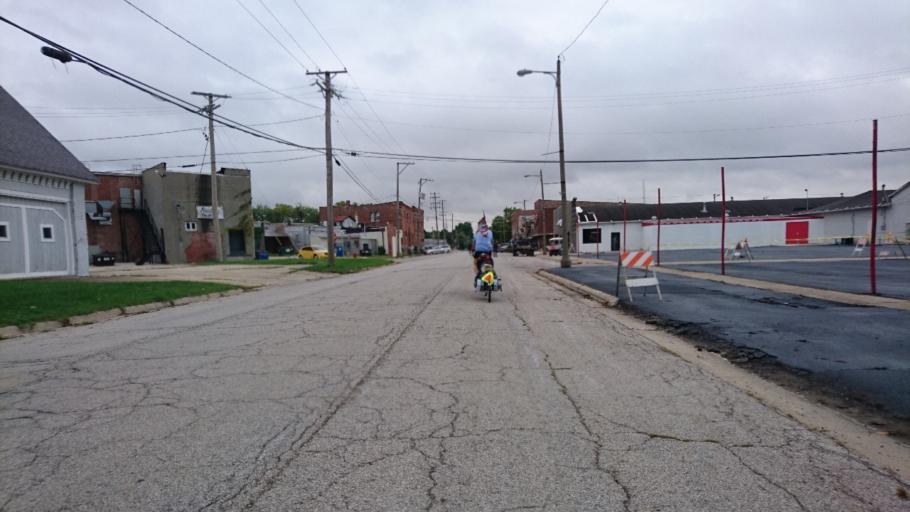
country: US
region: Illinois
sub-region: Livingston County
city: Dwight
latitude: 41.0922
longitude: -88.4259
